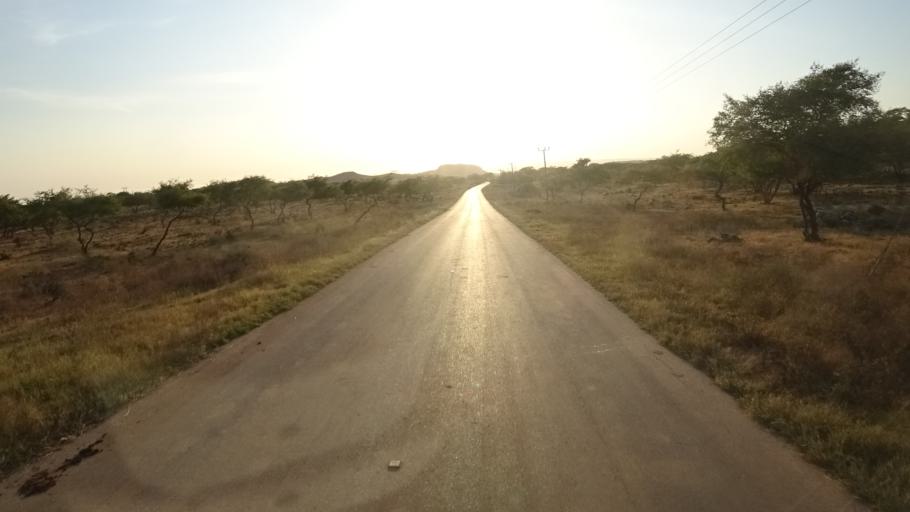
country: OM
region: Zufar
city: Salalah
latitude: 17.1485
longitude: 54.5960
